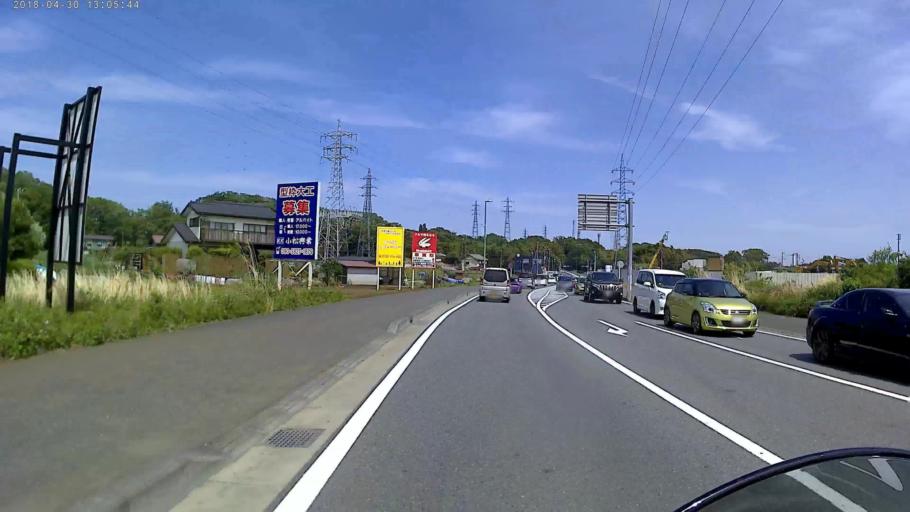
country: JP
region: Tokyo
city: Hachioji
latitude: 35.5896
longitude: 139.3096
